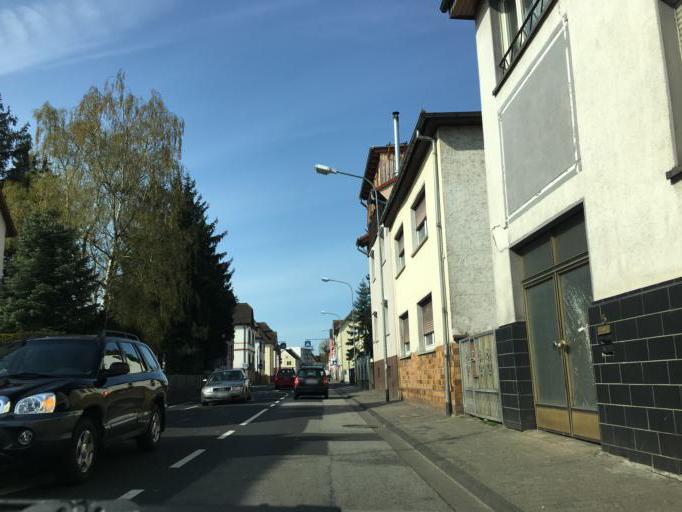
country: DE
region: Hesse
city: Obertshausen
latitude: 50.0741
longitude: 8.8550
